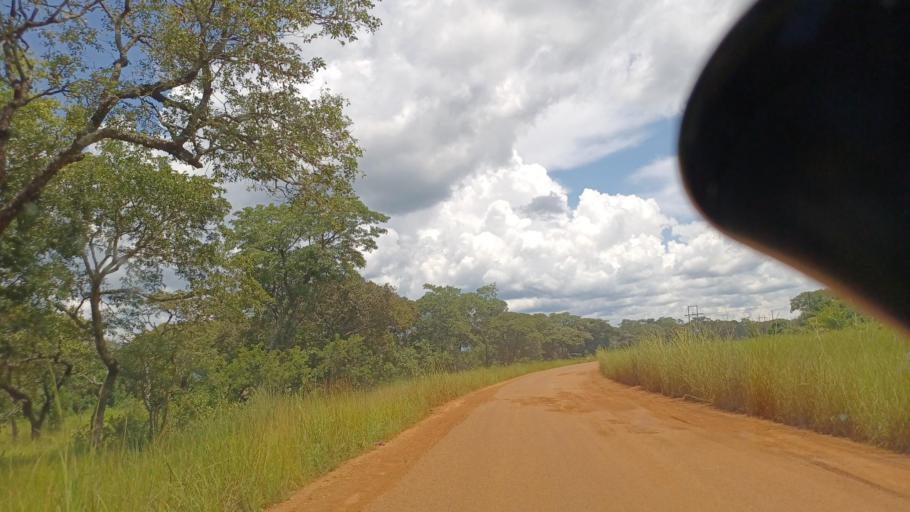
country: ZM
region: North-Western
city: Solwezi
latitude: -12.6955
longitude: 26.0399
